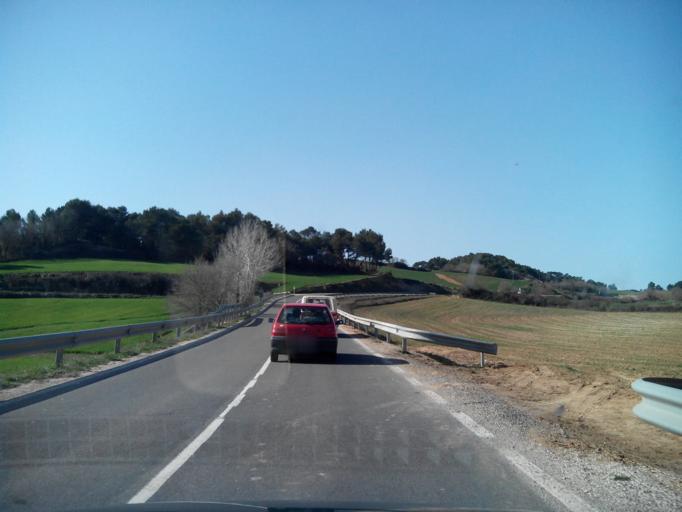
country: ES
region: Catalonia
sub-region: Provincia de Tarragona
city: Conesa
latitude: 41.4959
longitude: 1.3317
